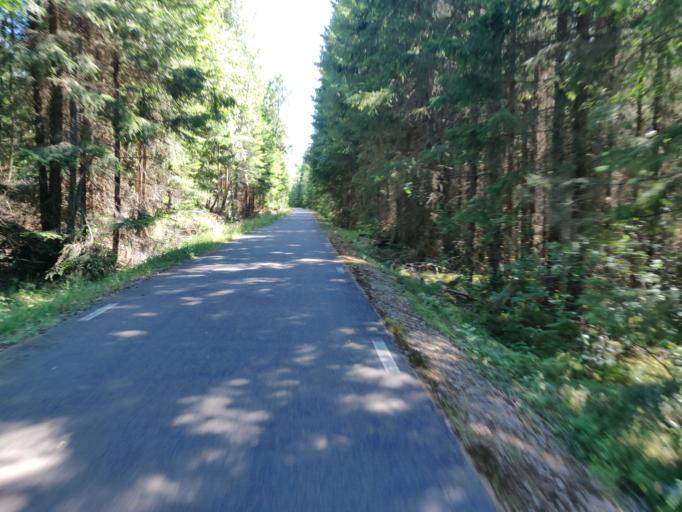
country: SE
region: Vaermland
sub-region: Munkfors Kommun
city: Munkfors
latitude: 59.9520
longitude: 13.5772
